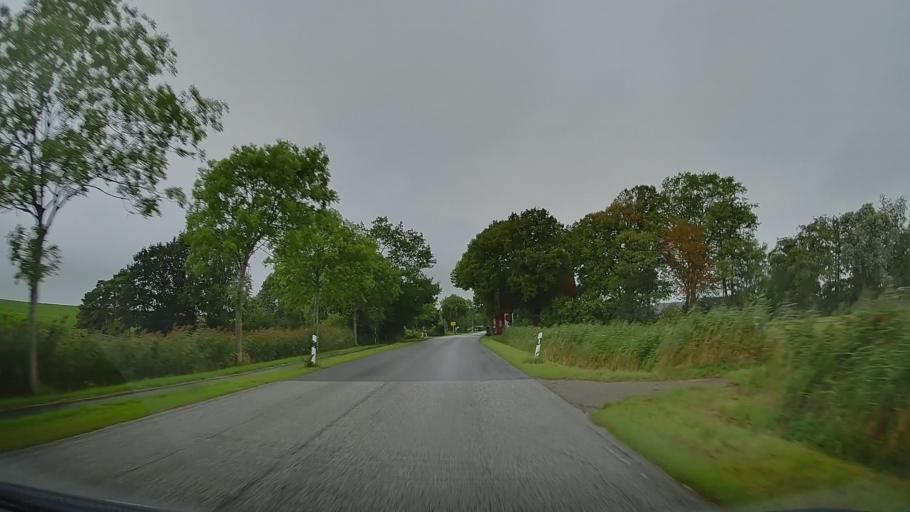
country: DE
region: Schleswig-Holstein
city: Sankt Margarethen
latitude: 53.8830
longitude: 9.2582
